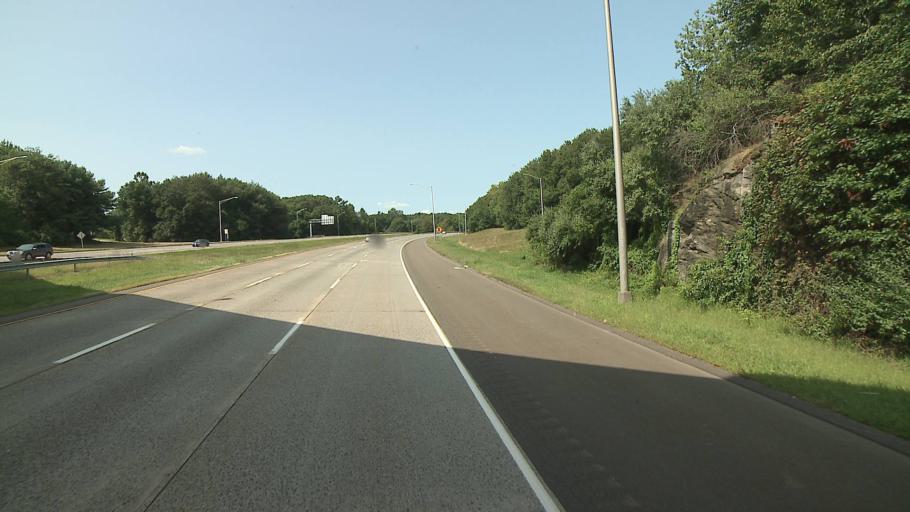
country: US
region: Connecticut
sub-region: Fairfield County
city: Trumbull
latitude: 41.2326
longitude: -73.1893
